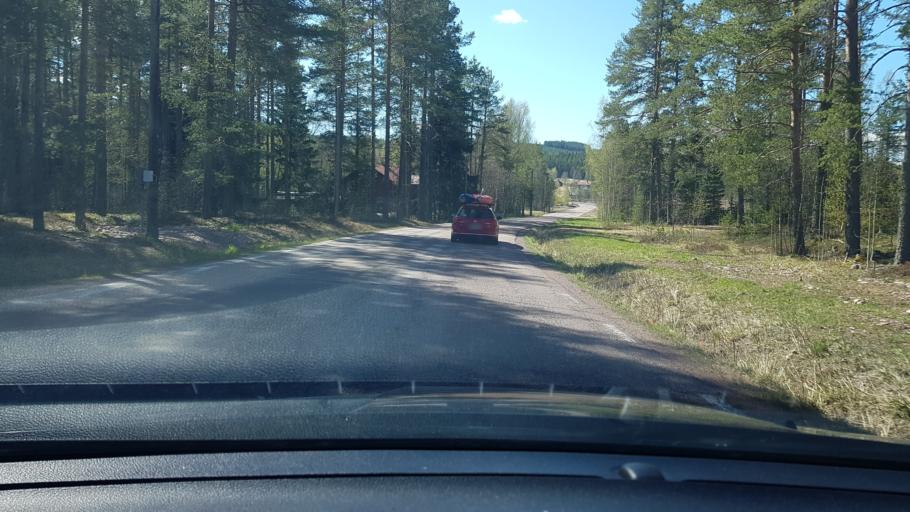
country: SE
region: Dalarna
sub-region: Alvdalens Kommun
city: AElvdalen
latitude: 61.1234
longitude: 14.1736
